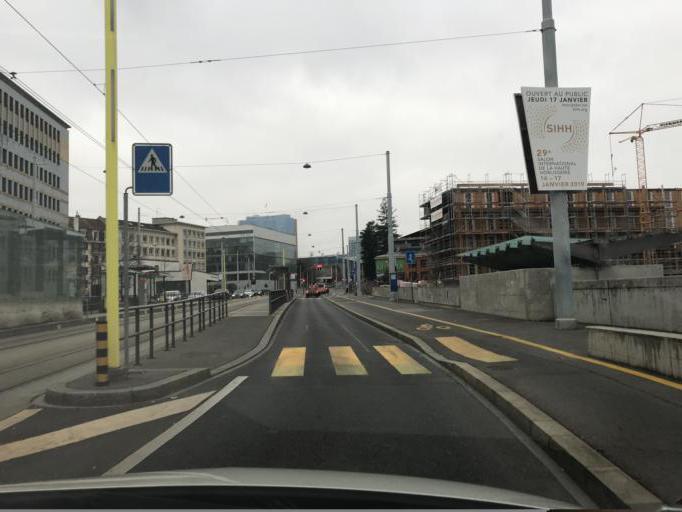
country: CH
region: Geneva
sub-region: Geneva
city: Geneve
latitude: 46.2209
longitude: 6.1421
